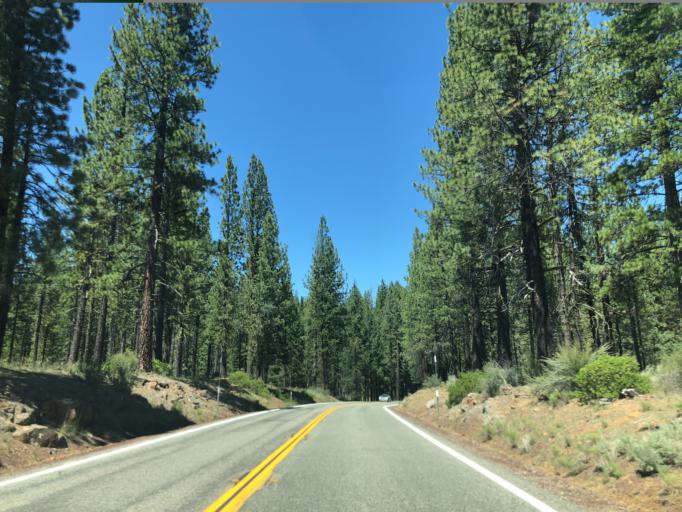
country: US
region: California
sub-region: Shasta County
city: Burney
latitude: 40.6414
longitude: -121.4721
